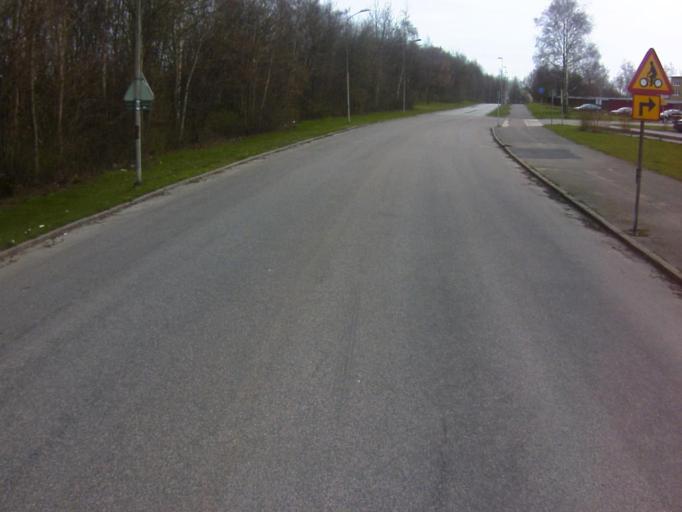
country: SE
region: Skane
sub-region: Kavlinge Kommun
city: Kaevlinge
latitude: 55.7973
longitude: 13.1039
